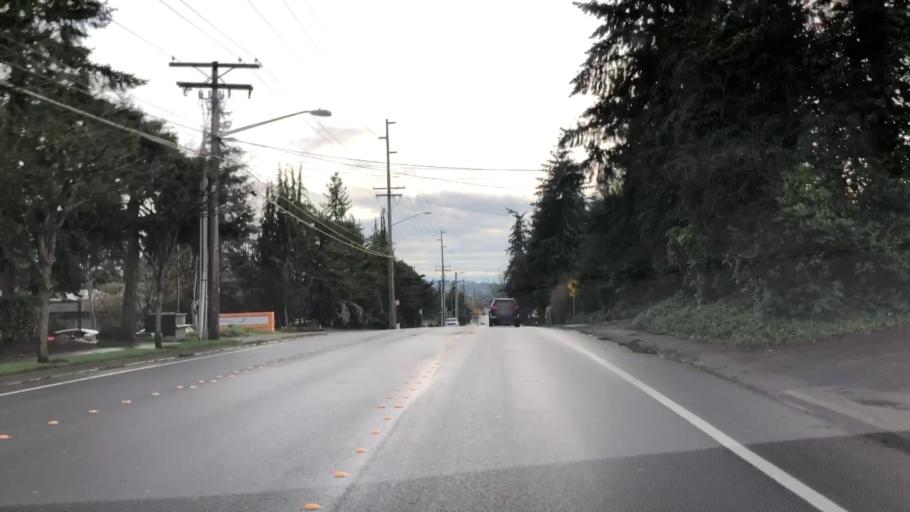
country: US
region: Washington
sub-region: King County
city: Bellevue
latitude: 47.6262
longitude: -122.1857
